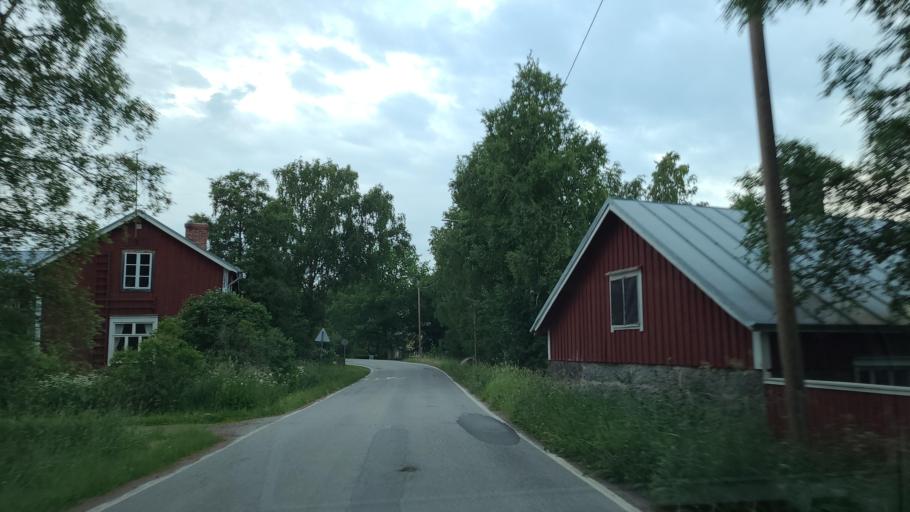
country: FI
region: Ostrobothnia
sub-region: Vaasa
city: Replot
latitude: 63.1799
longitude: 21.2812
